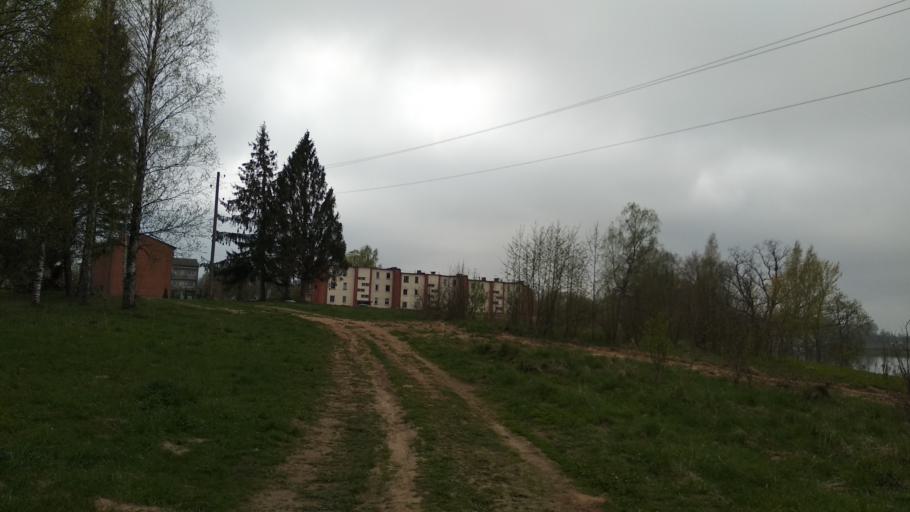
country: LV
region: Malpils
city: Malpils
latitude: 57.0140
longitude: 24.9526
